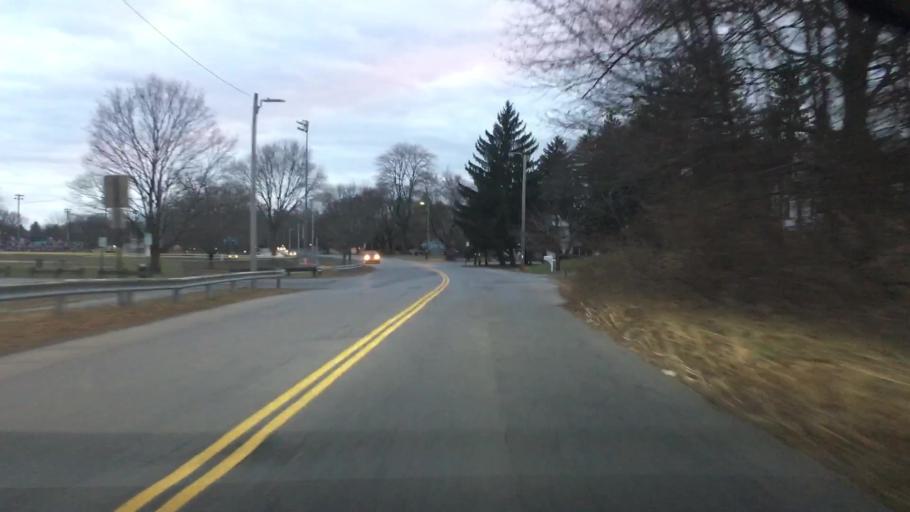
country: US
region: New York
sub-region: Dutchess County
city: Spackenkill
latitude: 41.6767
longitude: -73.9124
